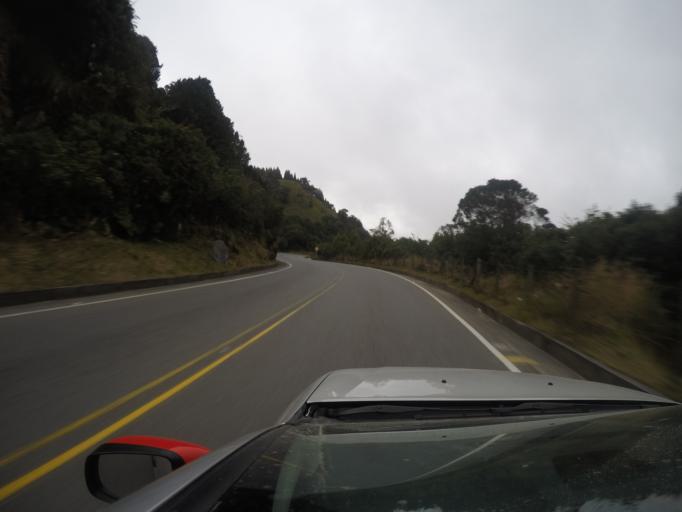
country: CO
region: Tolima
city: Herveo
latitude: 5.0571
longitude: -75.3181
